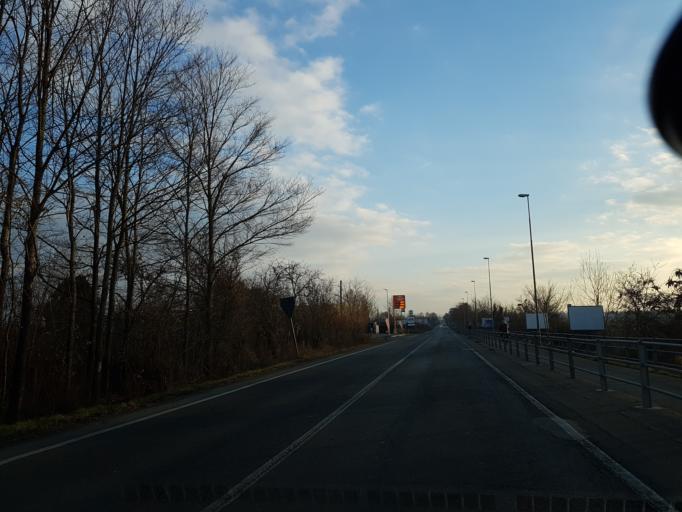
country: IT
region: Piedmont
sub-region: Provincia di Alessandria
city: Pozzolo Formigaro
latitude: 44.7850
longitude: 8.7888
